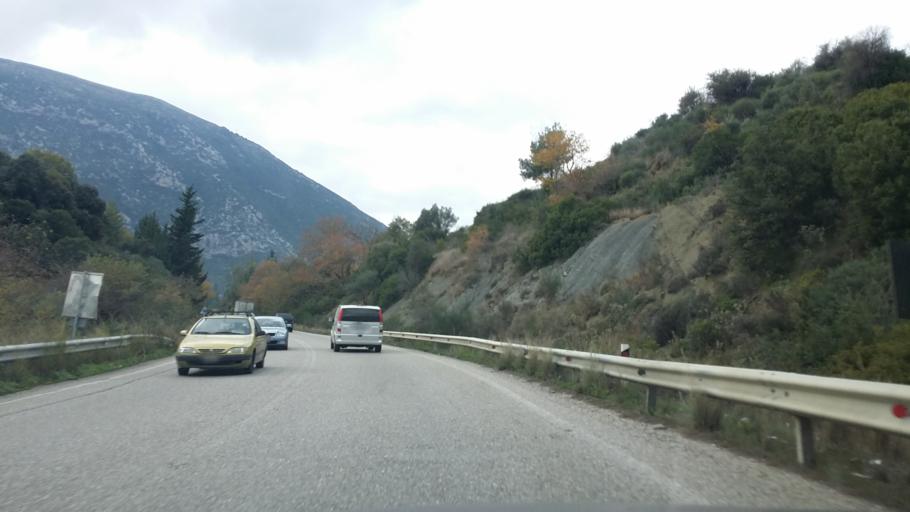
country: GR
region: West Greece
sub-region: Nomos Aitolias kai Akarnanias
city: Galatas
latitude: 38.3827
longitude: 21.6126
